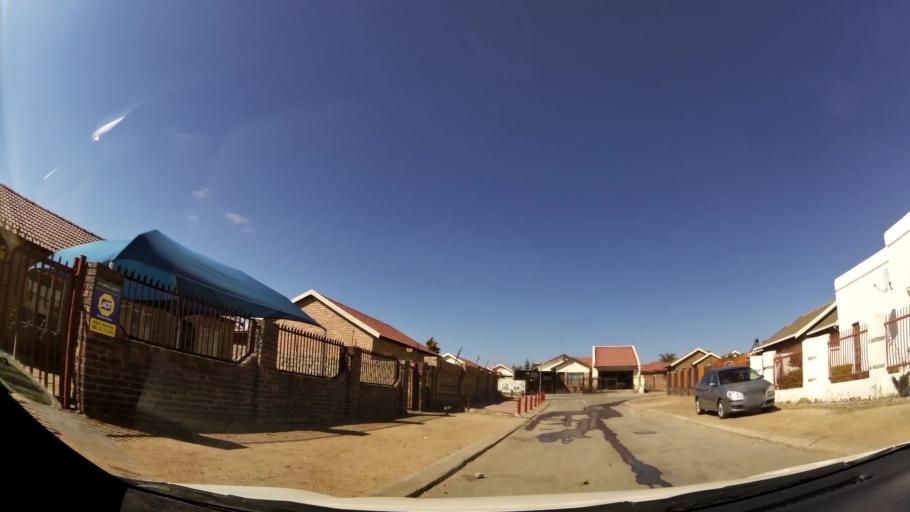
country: ZA
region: Limpopo
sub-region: Capricorn District Municipality
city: Polokwane
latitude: -23.8727
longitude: 29.4113
